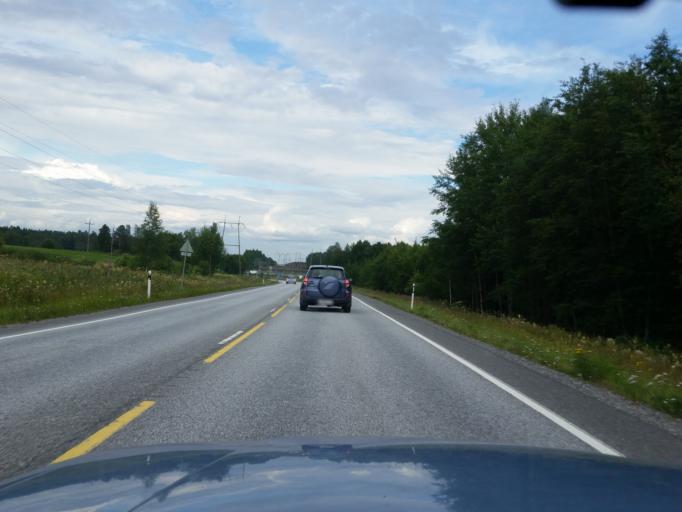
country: FI
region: Uusimaa
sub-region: Raaseporin
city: Karis
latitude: 60.0433
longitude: 23.6256
